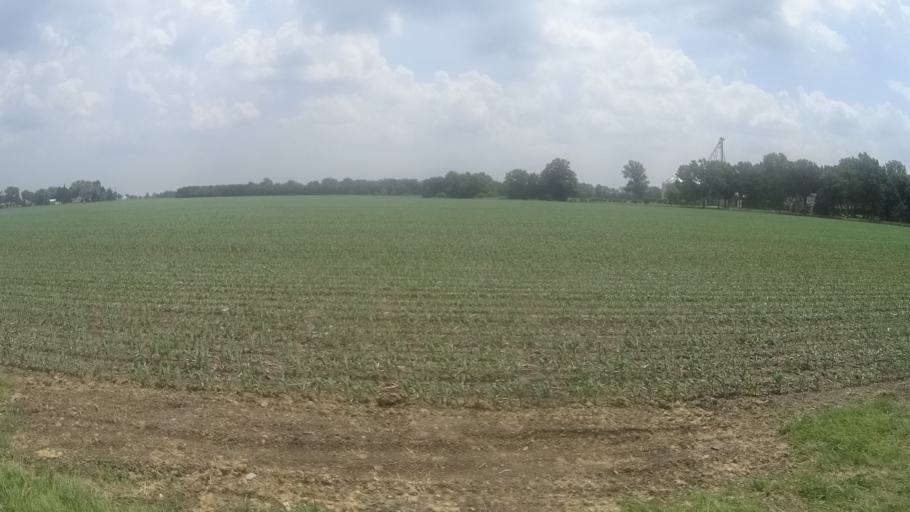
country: US
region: Ohio
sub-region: Huron County
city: Monroeville
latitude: 41.3207
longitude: -82.6931
